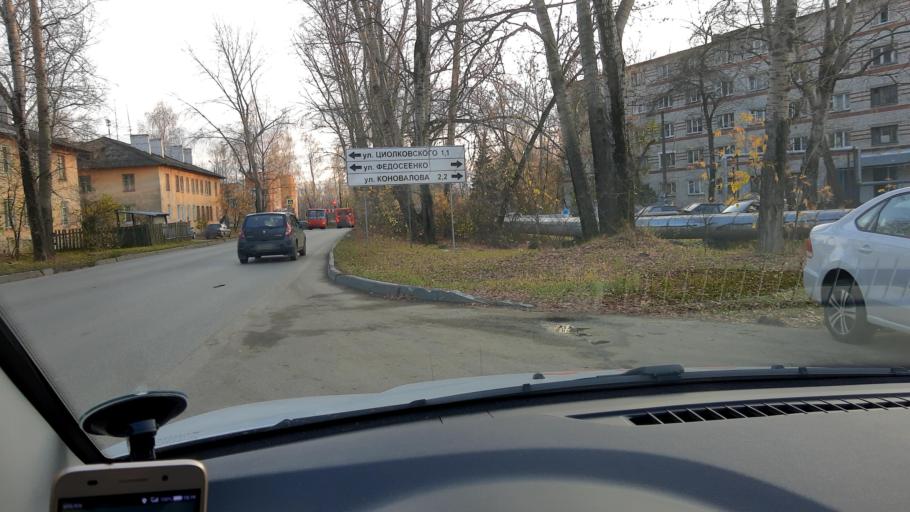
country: RU
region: Nizjnij Novgorod
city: Gorbatovka
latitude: 56.3424
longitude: 43.8238
